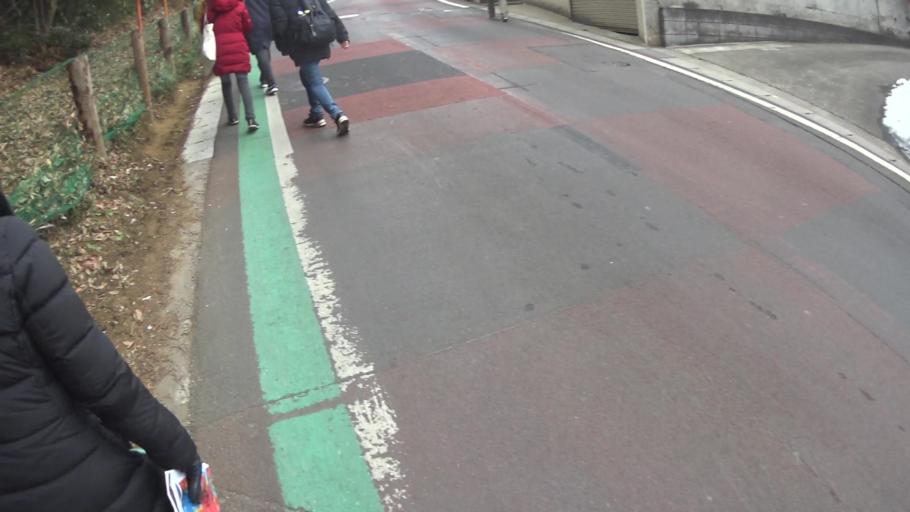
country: JP
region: Chiba
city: Funabashi
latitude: 35.7516
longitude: 139.9900
